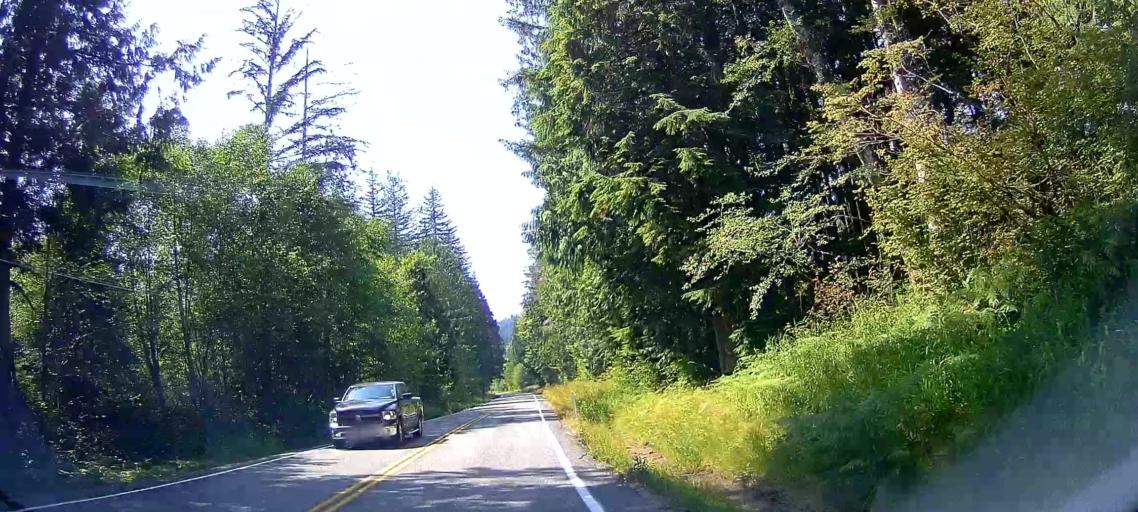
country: US
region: Washington
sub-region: Snohomish County
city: Bryant
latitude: 48.3434
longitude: -122.0952
